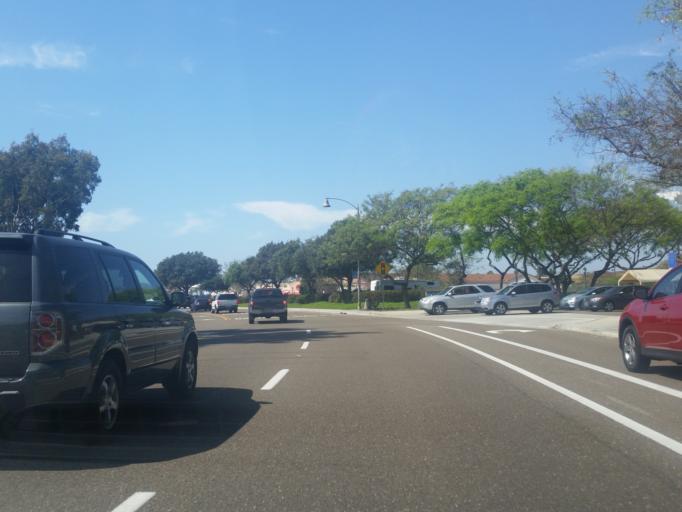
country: US
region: California
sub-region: San Diego County
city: Carlsbad
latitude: 33.1235
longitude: -117.3193
